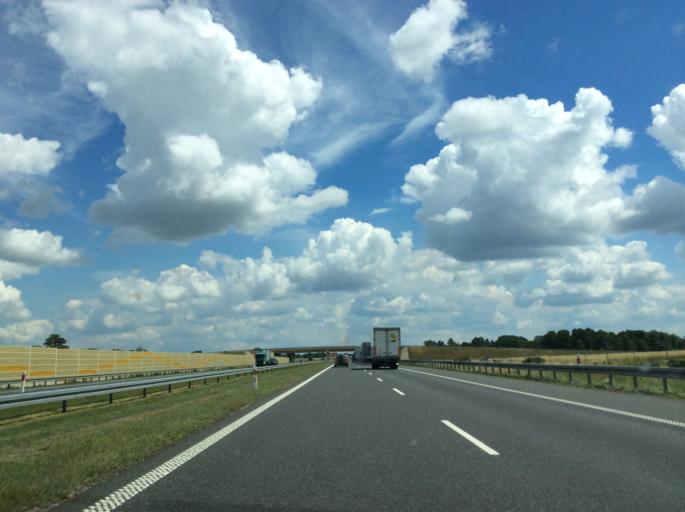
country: PL
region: Lodz Voivodeship
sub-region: Powiat poddebicki
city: Dalikow
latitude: 51.9681
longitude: 19.1013
